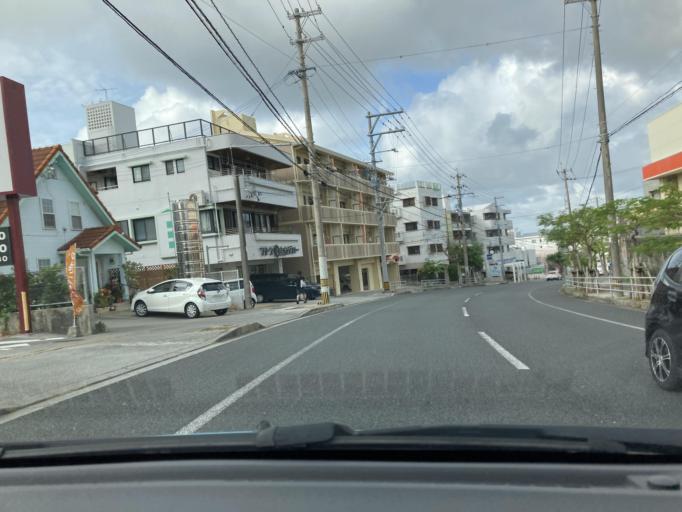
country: JP
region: Okinawa
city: Tomigusuku
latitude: 26.1883
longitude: 127.6731
